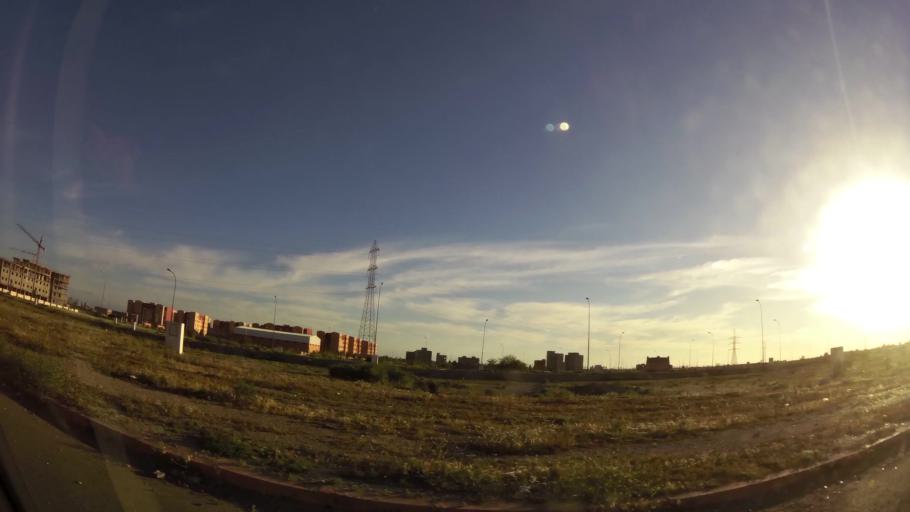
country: MA
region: Marrakech-Tensift-Al Haouz
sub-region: Marrakech
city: Marrakesh
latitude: 31.7444
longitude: -8.1259
